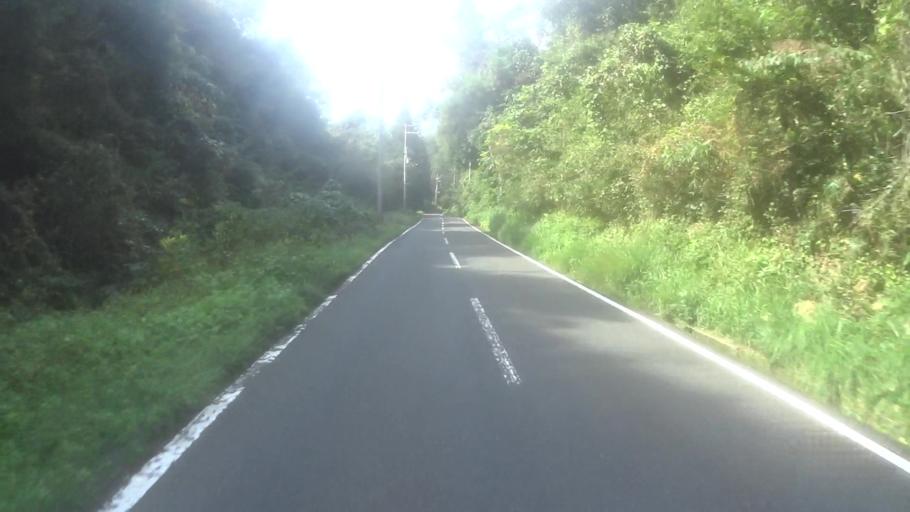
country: JP
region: Kyoto
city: Miyazu
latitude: 35.5870
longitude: 135.1250
